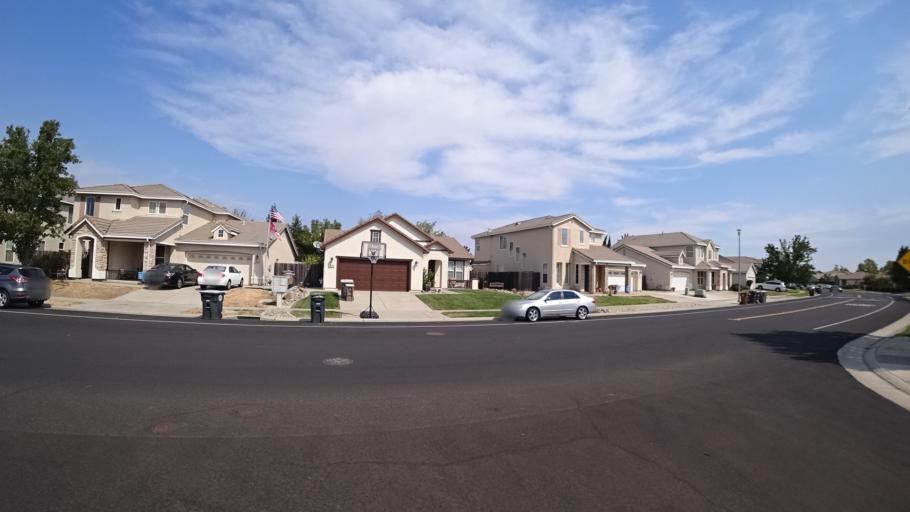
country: US
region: California
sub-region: Sacramento County
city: Laguna
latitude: 38.3878
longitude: -121.4468
